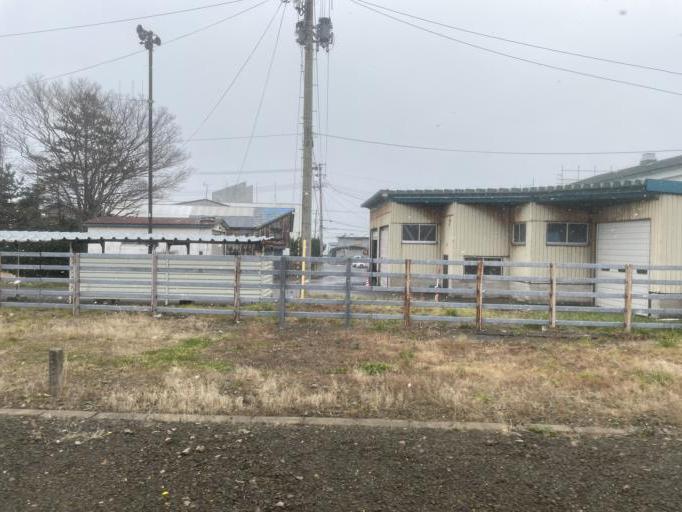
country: JP
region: Aomori
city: Aomori Shi
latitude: 40.9694
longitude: 140.6546
